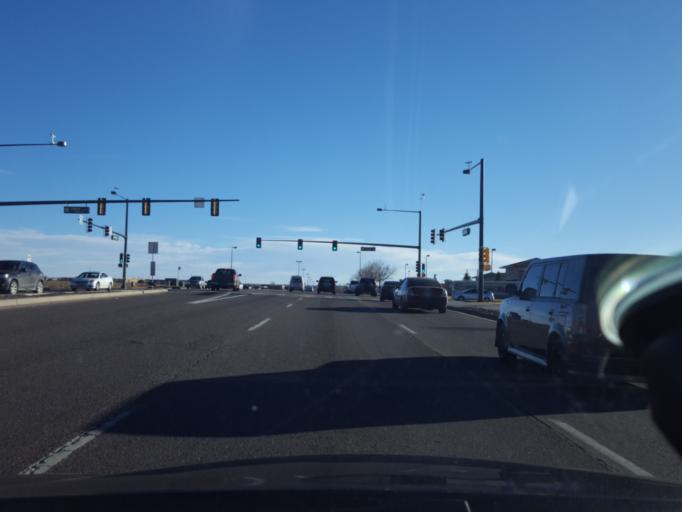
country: US
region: Colorado
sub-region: Adams County
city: Aurora
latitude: 39.7698
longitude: -104.7723
